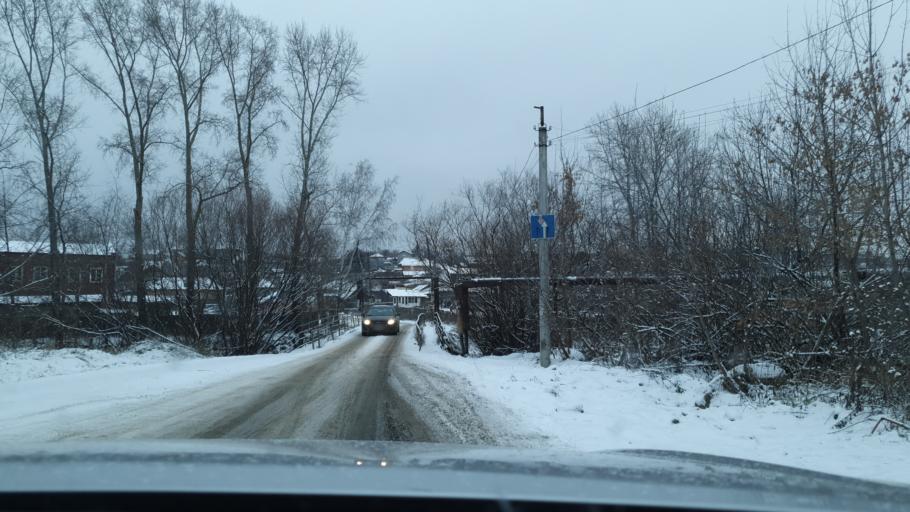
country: RU
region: Sverdlovsk
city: Istok
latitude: 56.7491
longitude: 60.7001
